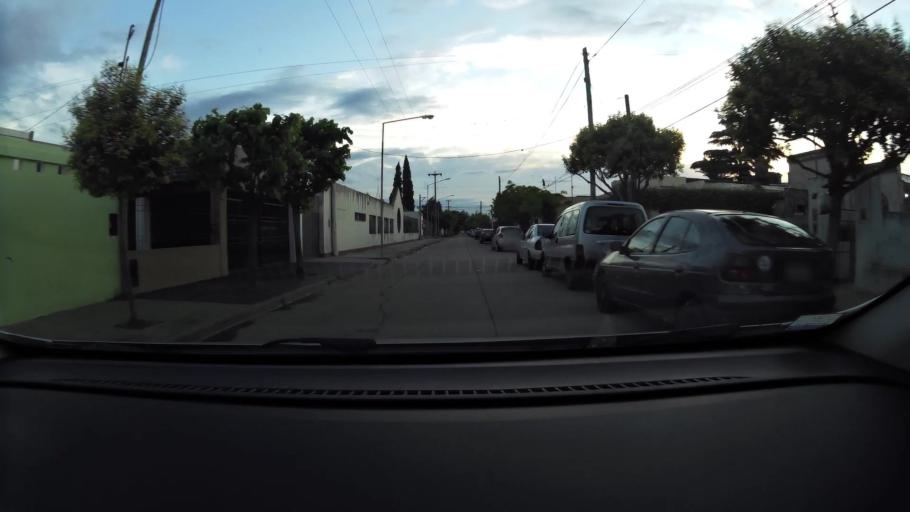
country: AR
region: Buenos Aires
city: San Nicolas de los Arroyos
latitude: -33.3250
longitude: -60.2253
